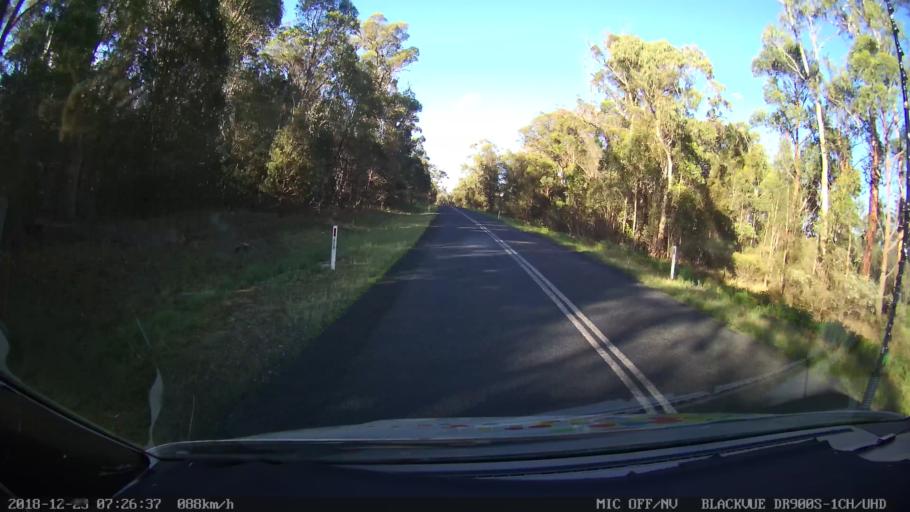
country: AU
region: New South Wales
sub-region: Armidale Dumaresq
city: Enmore
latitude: -30.4925
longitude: 152.1961
